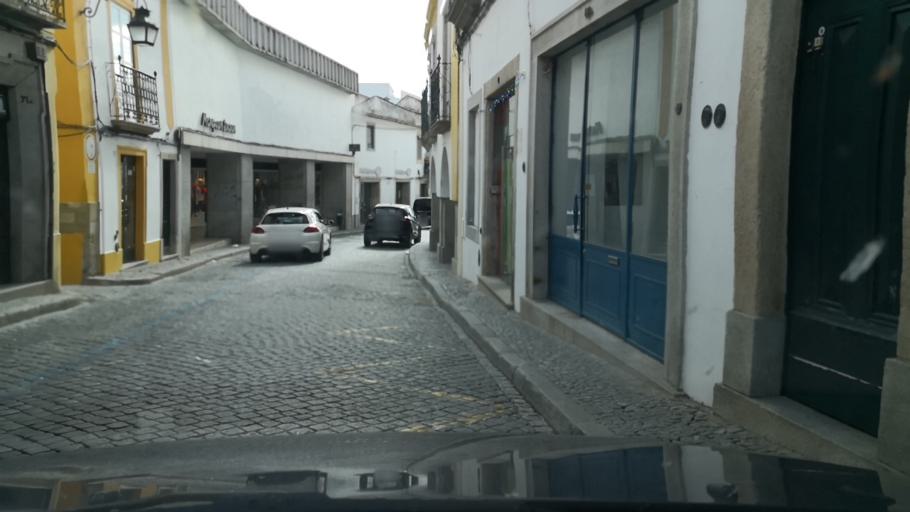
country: PT
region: Evora
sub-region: Evora
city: Evora
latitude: 38.5709
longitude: -7.9111
